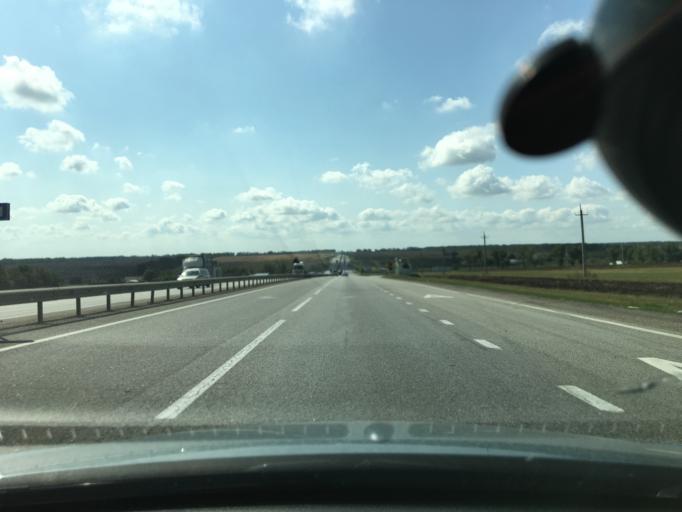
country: RU
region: Krasnodarskiy
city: Krasnoye
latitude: 46.7750
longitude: 39.6637
